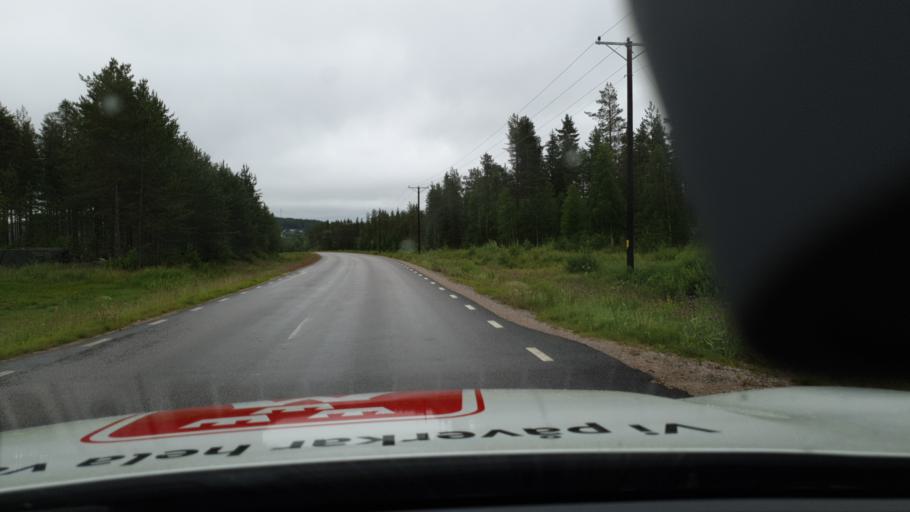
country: SE
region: Norrbotten
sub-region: Overtornea Kommun
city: OEvertornea
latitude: 66.3945
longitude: 23.6017
